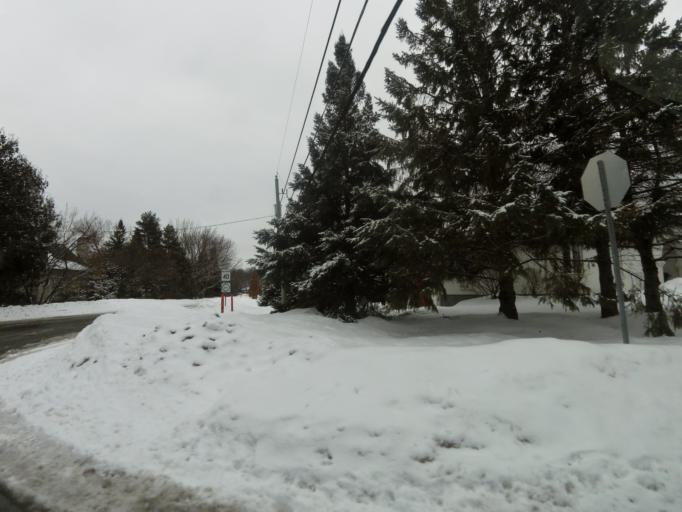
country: CA
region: Quebec
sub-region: Outaouais
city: Gatineau
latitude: 45.4609
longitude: -75.6165
